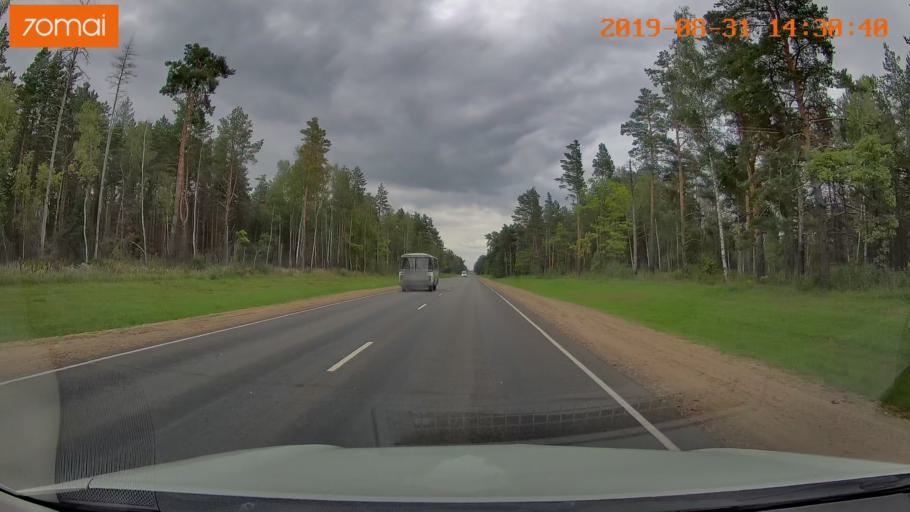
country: RU
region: Smolensk
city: Yekimovichi
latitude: 54.1330
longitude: 33.3556
